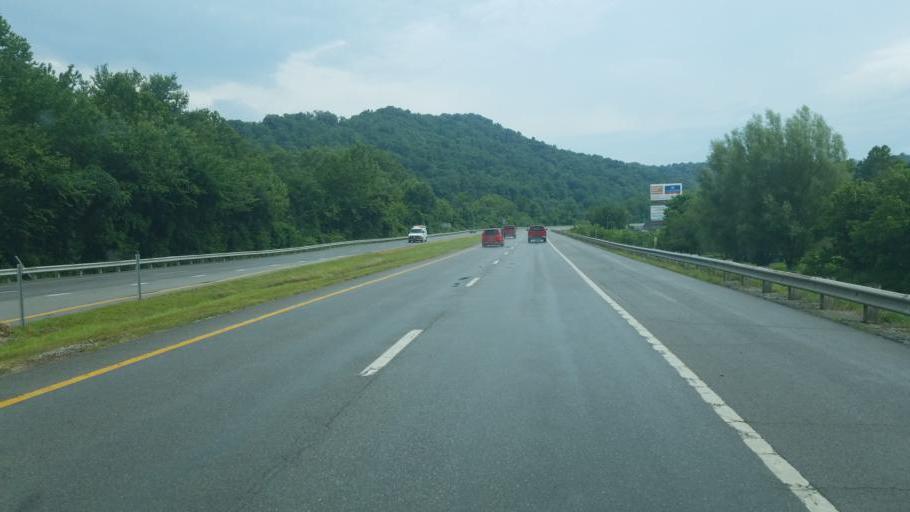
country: US
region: West Virginia
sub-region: Logan County
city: Chapmanville
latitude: 37.9588
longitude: -82.0189
